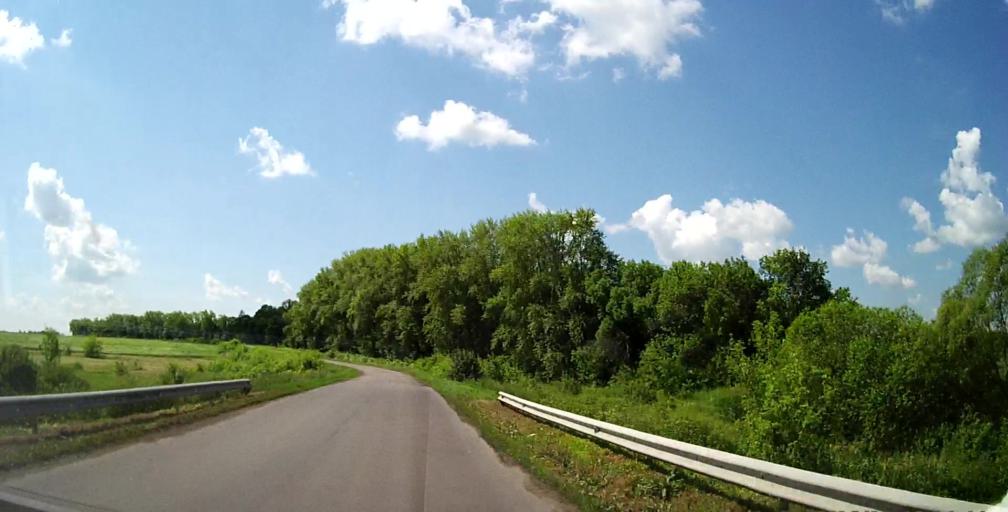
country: RU
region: Lipetsk
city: Chaplygin
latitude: 53.3041
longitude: 39.9521
